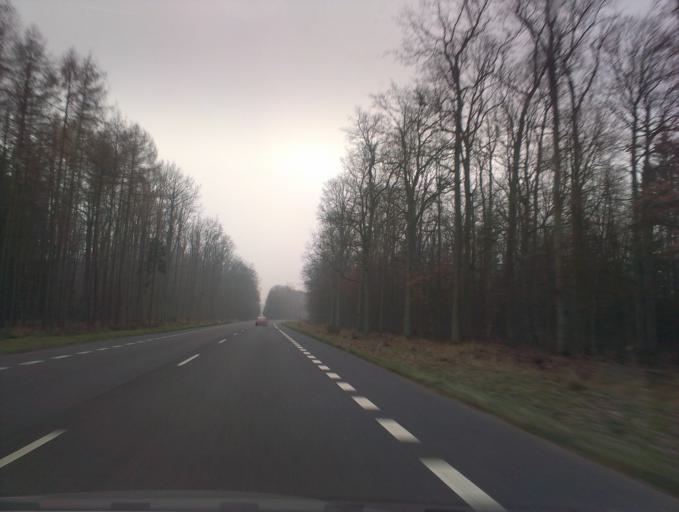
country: PL
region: Greater Poland Voivodeship
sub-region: Powiat chodzieski
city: Budzyn
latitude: 52.9151
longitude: 16.9724
